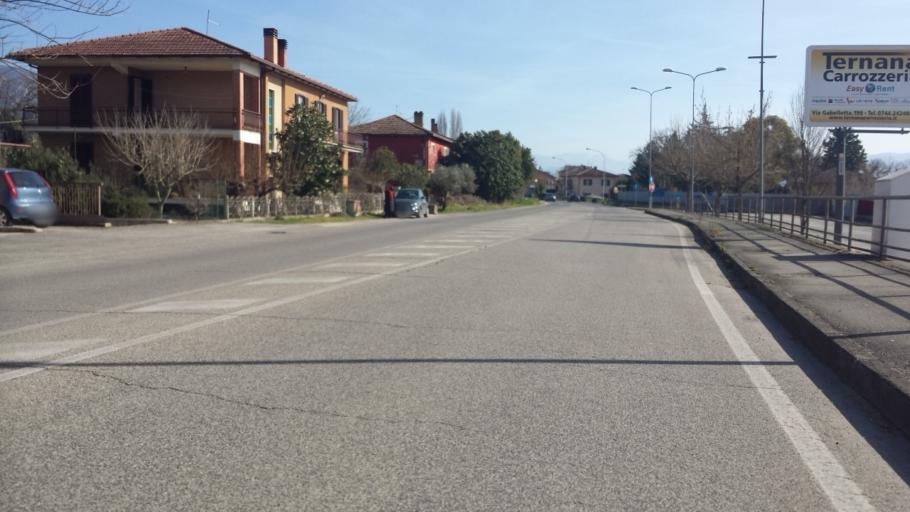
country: IT
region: Umbria
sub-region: Provincia di Terni
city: San Gemini
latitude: 42.5911
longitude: 12.5734
